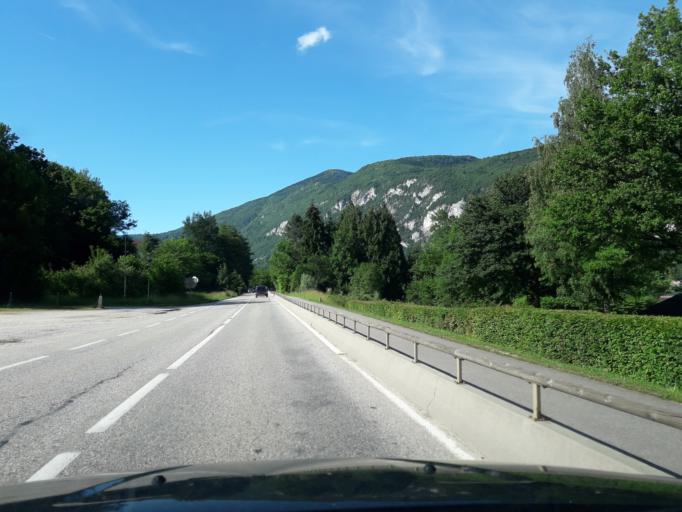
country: FR
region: Rhone-Alpes
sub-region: Departement de la Savoie
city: Novalaise
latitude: 45.5678
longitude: 5.7941
